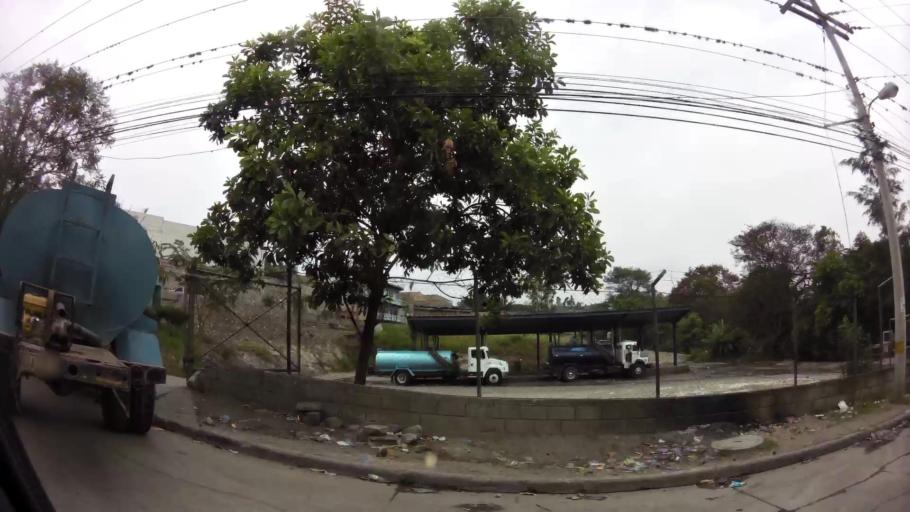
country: HN
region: Francisco Morazan
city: Tegucigalpa
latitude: 14.0693
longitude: -87.2363
